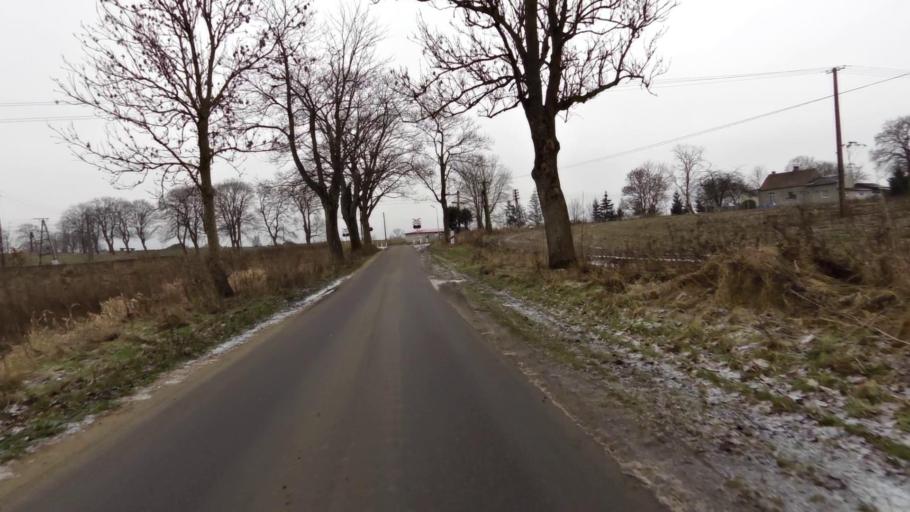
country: PL
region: West Pomeranian Voivodeship
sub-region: Powiat szczecinecki
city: Szczecinek
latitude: 53.6603
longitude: 16.6263
